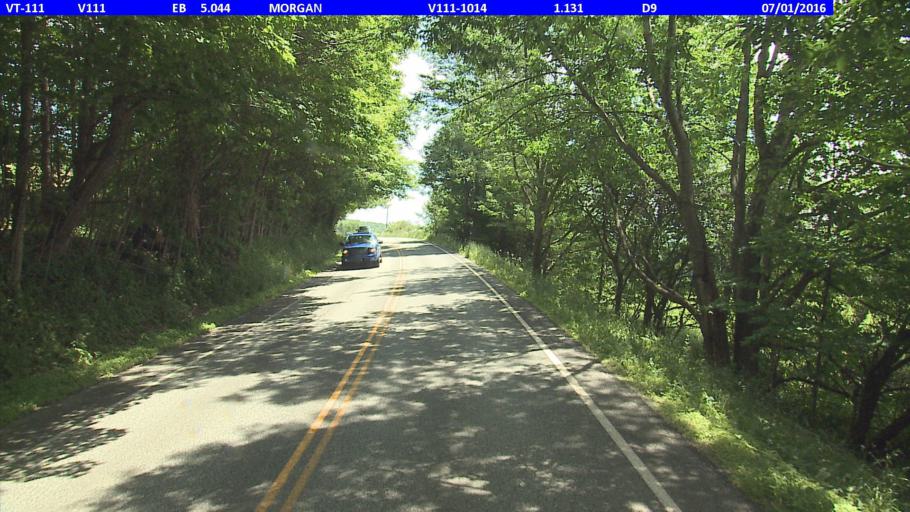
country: US
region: Vermont
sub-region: Orleans County
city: Newport
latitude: 44.9242
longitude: -72.0446
